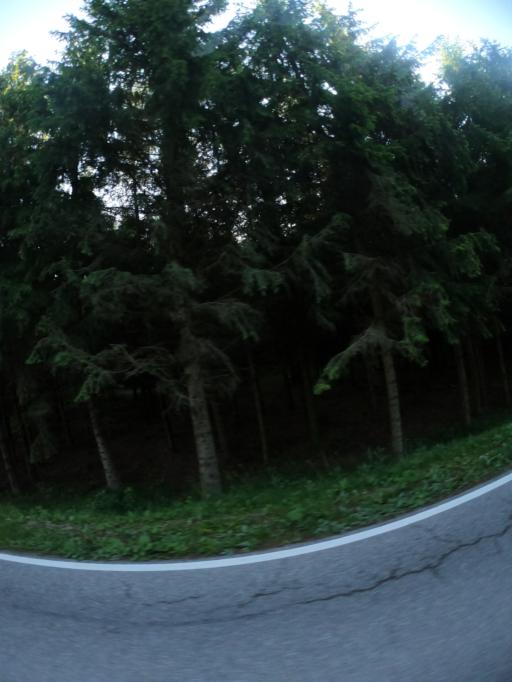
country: DE
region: Bavaria
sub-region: Upper Bavaria
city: Inning am Holz
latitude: 48.3406
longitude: 12.0722
